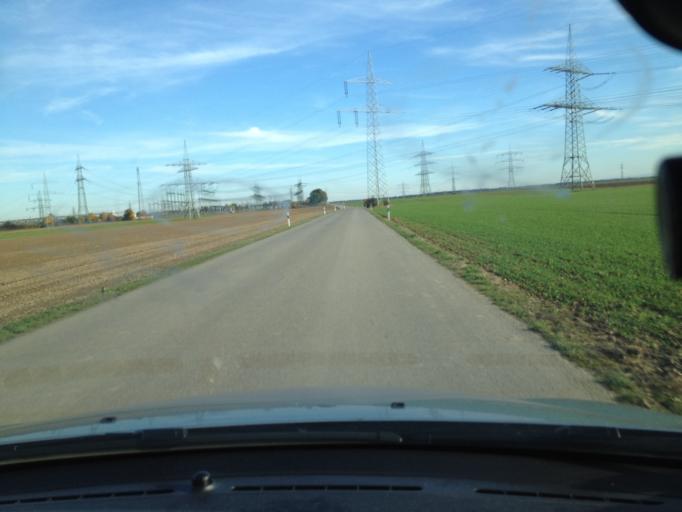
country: DE
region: Bavaria
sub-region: Swabia
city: Oberottmarshausen
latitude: 48.2390
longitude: 10.8311
